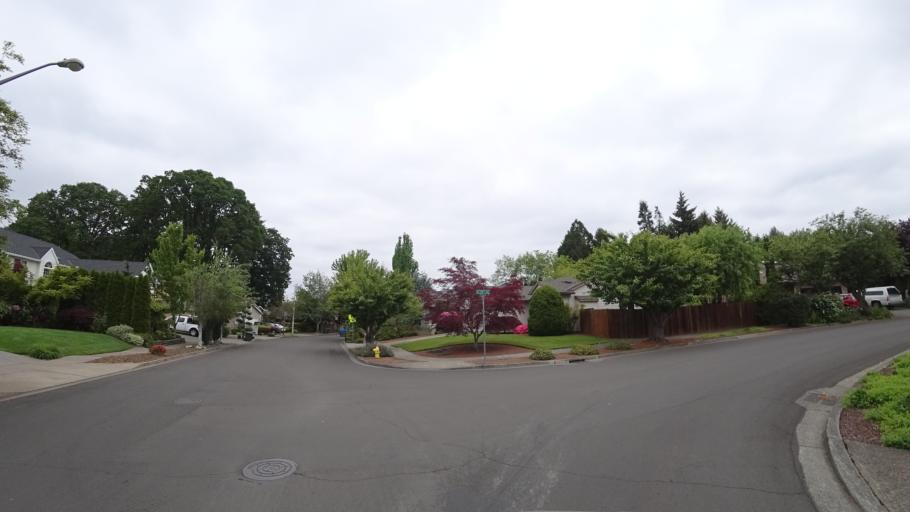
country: US
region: Oregon
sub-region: Washington County
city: Aloha
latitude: 45.5021
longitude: -122.9085
